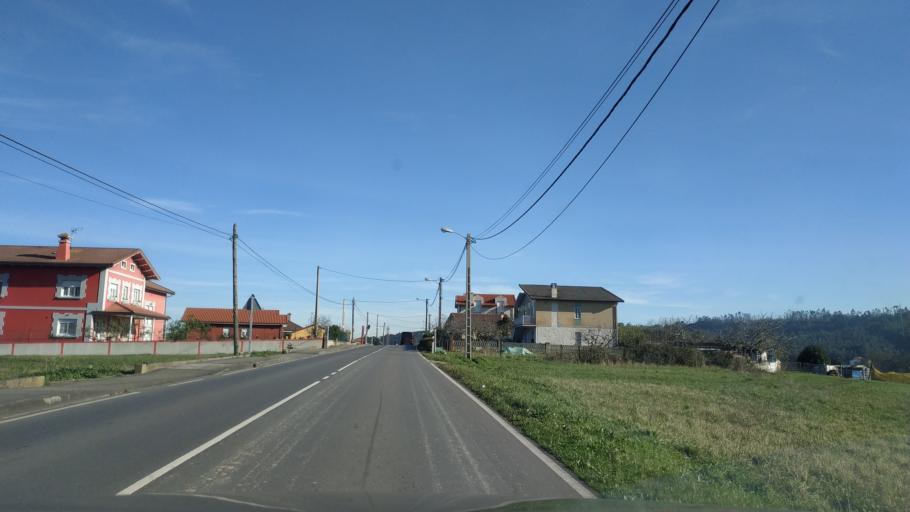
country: ES
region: Asturias
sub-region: Province of Asturias
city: Corvera de Asturias
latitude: 43.5386
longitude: -5.8867
